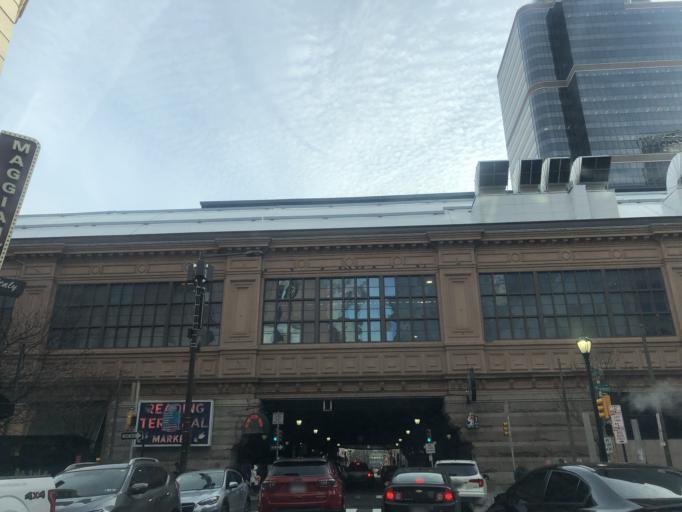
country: US
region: Pennsylvania
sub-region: Philadelphia County
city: Philadelphia
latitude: 39.9530
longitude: -75.1601
